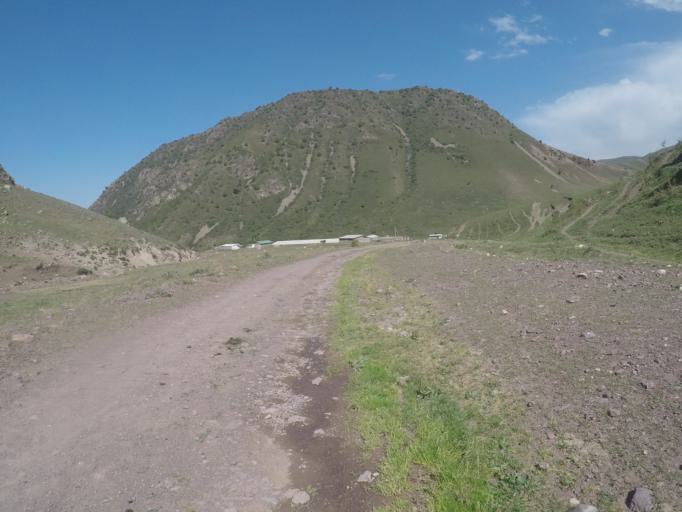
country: KG
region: Chuy
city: Bishkek
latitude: 42.6439
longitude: 74.6128
